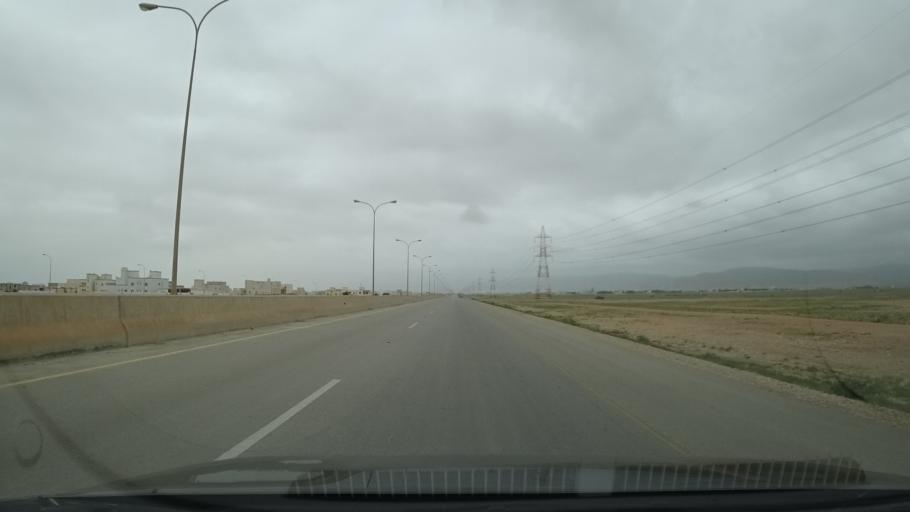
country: OM
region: Zufar
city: Salalah
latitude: 17.1036
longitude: 54.2093
